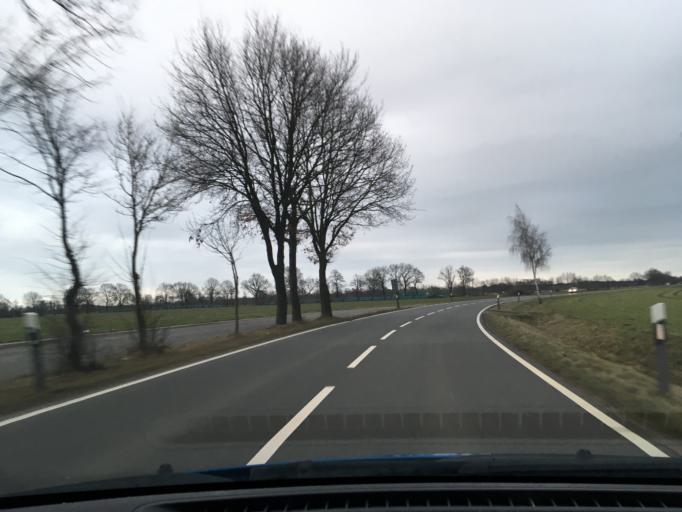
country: DE
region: Lower Saxony
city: Brietlingen
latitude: 53.3442
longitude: 10.4280
